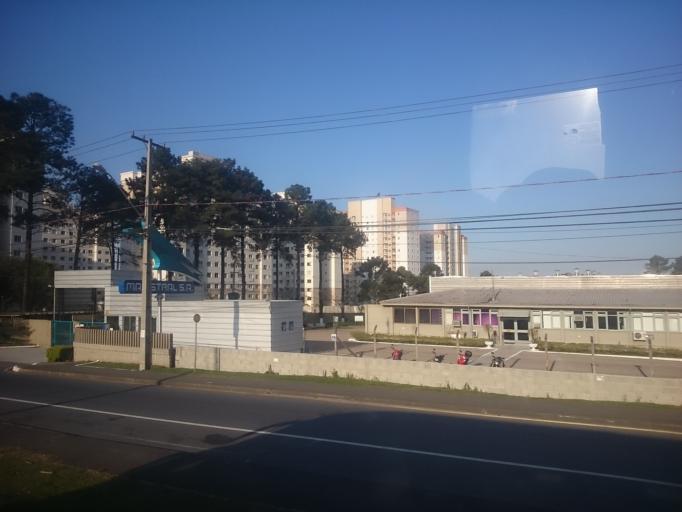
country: BR
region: Parana
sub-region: Sao Jose Dos Pinhais
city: Sao Jose dos Pinhais
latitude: -25.5151
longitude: -49.2904
